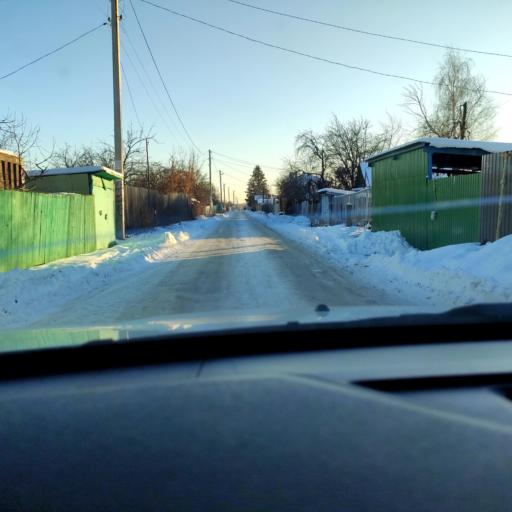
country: RU
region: Samara
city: Petra-Dubrava
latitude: 53.2862
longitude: 50.2913
